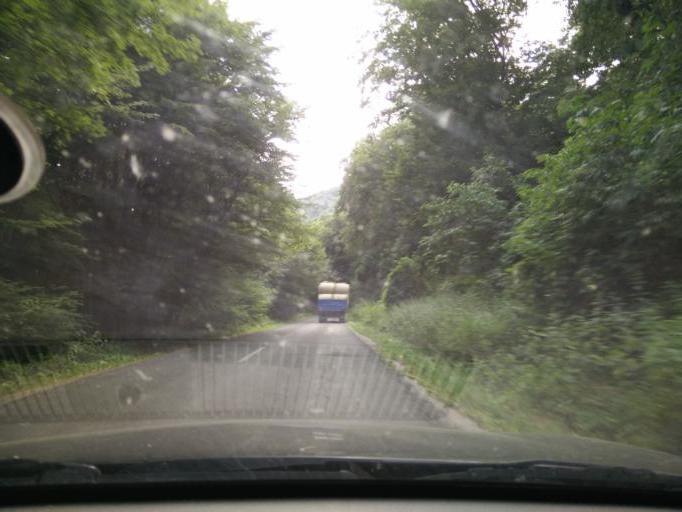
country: HU
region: Komarom-Esztergom
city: Tardos
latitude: 47.6788
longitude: 18.4366
